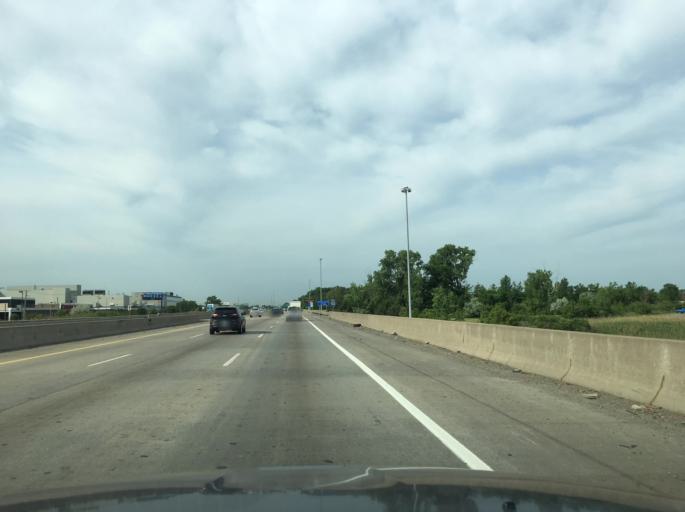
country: US
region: Michigan
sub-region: Wayne County
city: Melvindale
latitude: 42.2957
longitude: -83.1874
